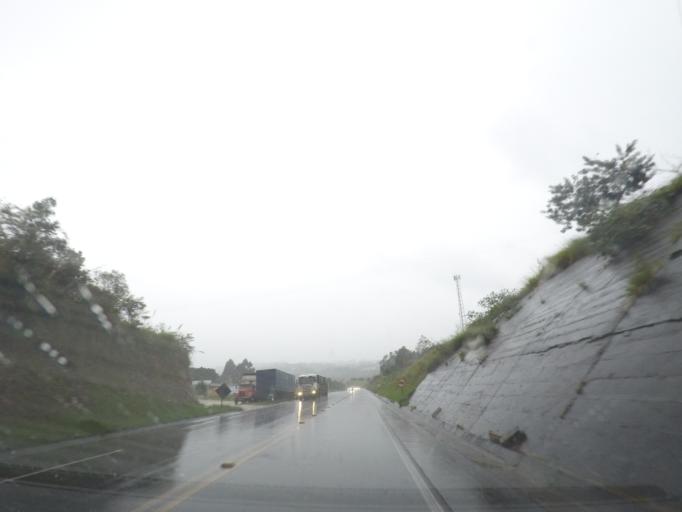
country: BR
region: Parana
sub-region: Almirante Tamandare
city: Almirante Tamandare
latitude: -25.3538
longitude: -49.2913
